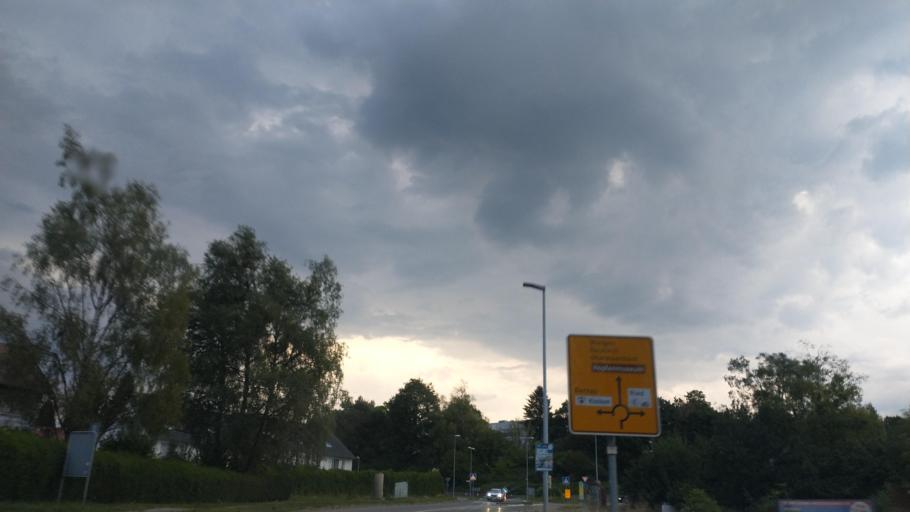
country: DE
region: Baden-Wuerttemberg
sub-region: Tuebingen Region
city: Tettnang
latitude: 47.6711
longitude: 9.5946
